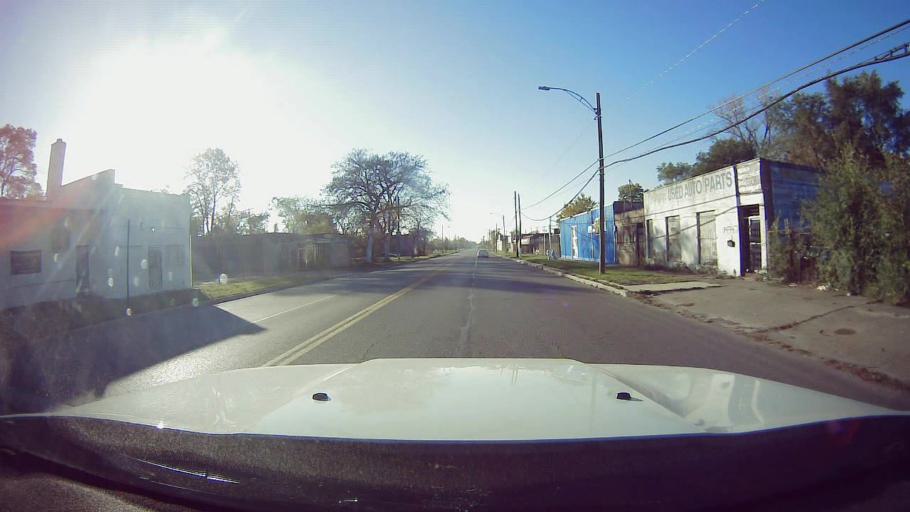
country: US
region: Michigan
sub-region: Oakland County
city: Oak Park
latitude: 42.4000
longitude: -83.1693
